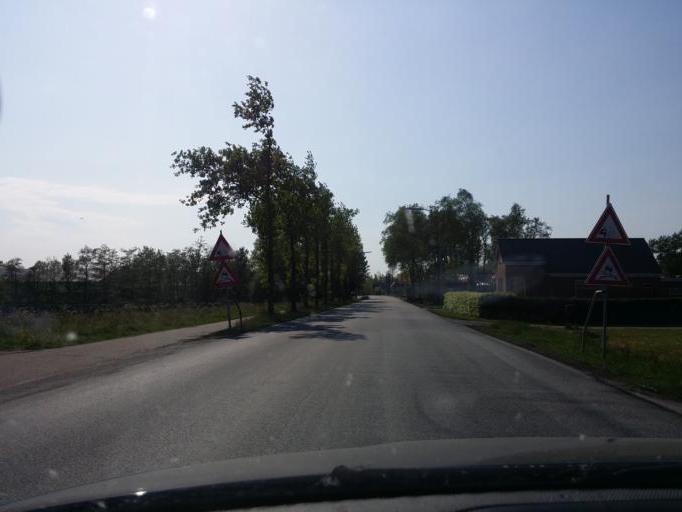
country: NL
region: Groningen
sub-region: Gemeente Zuidhorn
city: Grijpskerk
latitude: 53.2213
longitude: 6.3202
